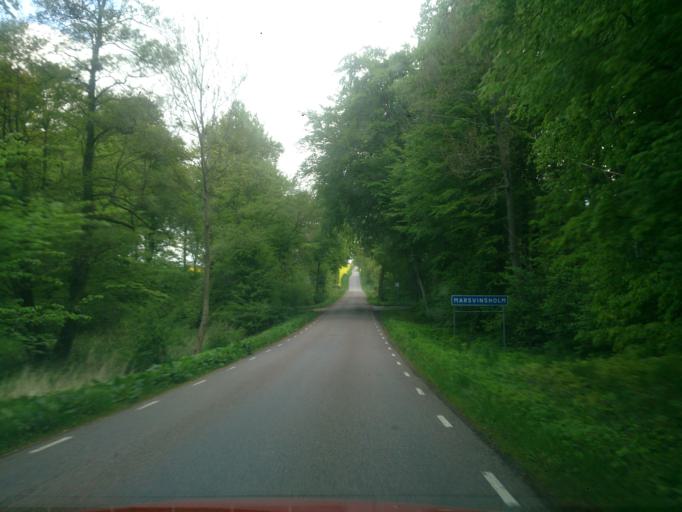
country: SE
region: Skane
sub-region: Ystads Kommun
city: Ystad
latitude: 55.4552
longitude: 13.7104
